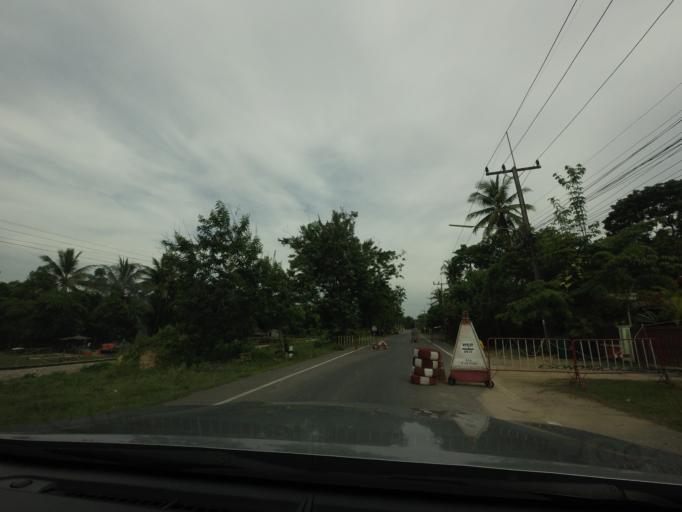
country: TH
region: Yala
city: Raman
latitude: 6.4519
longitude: 101.4496
